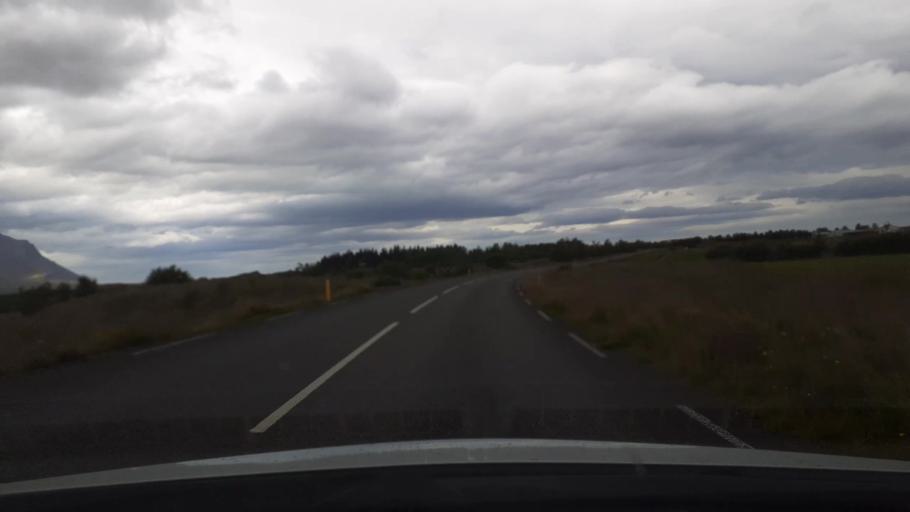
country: IS
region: West
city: Borgarnes
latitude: 64.5594
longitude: -21.7484
